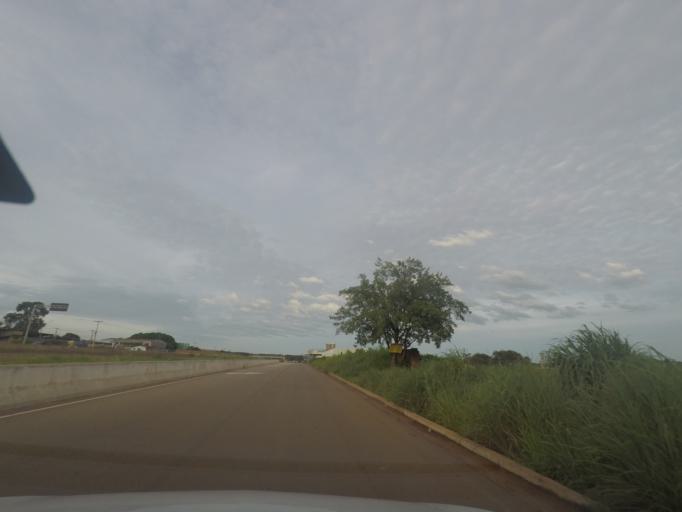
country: BR
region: Goias
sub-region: Goiania
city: Goiania
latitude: -16.7231
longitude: -49.3763
